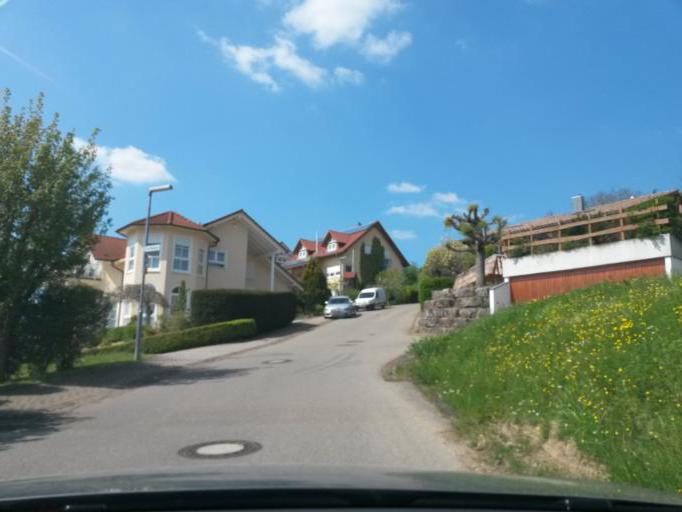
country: DE
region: Baden-Wuerttemberg
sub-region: Karlsruhe Region
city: Birkenfeld
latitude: 48.8982
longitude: 8.6012
